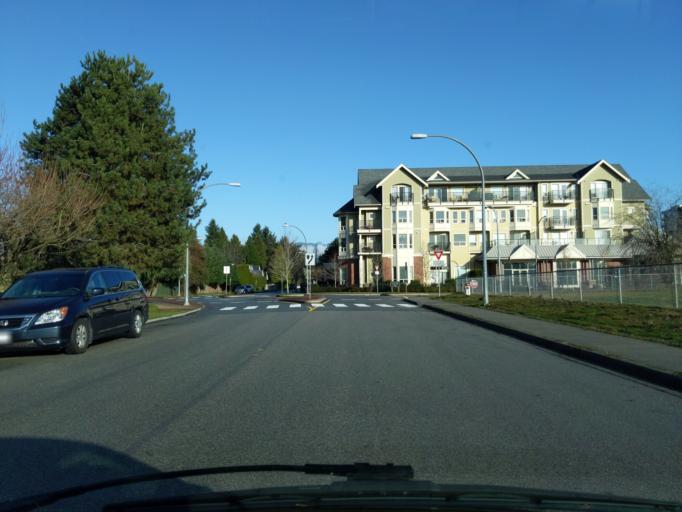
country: CA
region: British Columbia
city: Pitt Meadows
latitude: 49.2196
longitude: -122.6935
